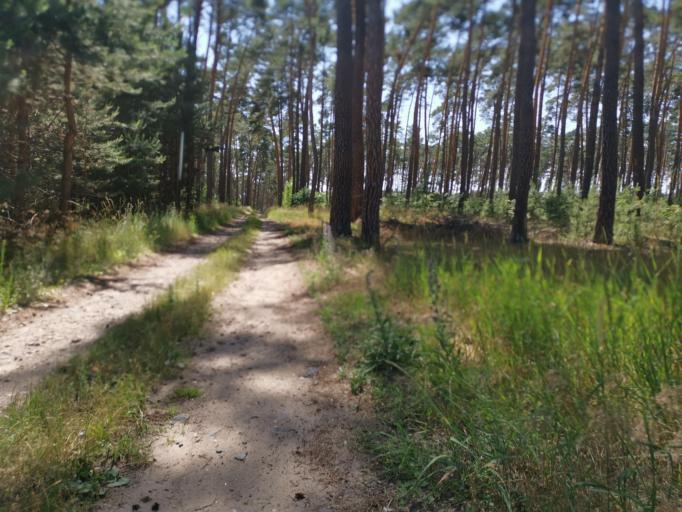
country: CZ
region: South Moravian
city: Rohatec
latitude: 48.9005
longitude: 17.2094
